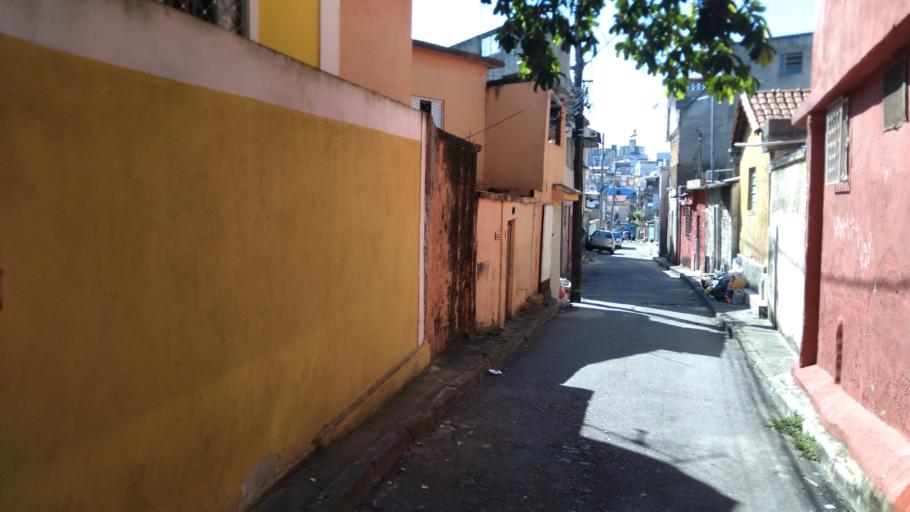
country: BR
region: Minas Gerais
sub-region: Belo Horizonte
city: Belo Horizonte
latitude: -19.8670
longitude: -43.9226
